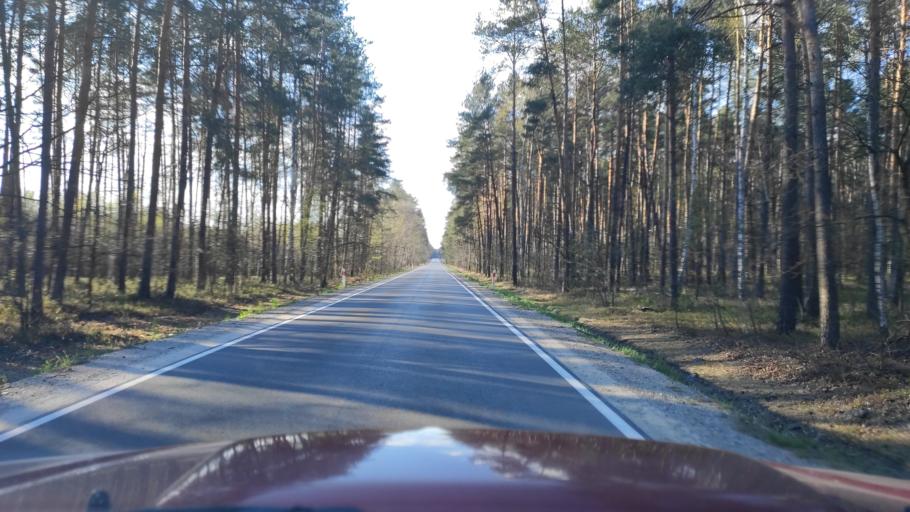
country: PL
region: Masovian Voivodeship
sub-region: Powiat zwolenski
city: Zwolen
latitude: 51.3913
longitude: 21.5484
